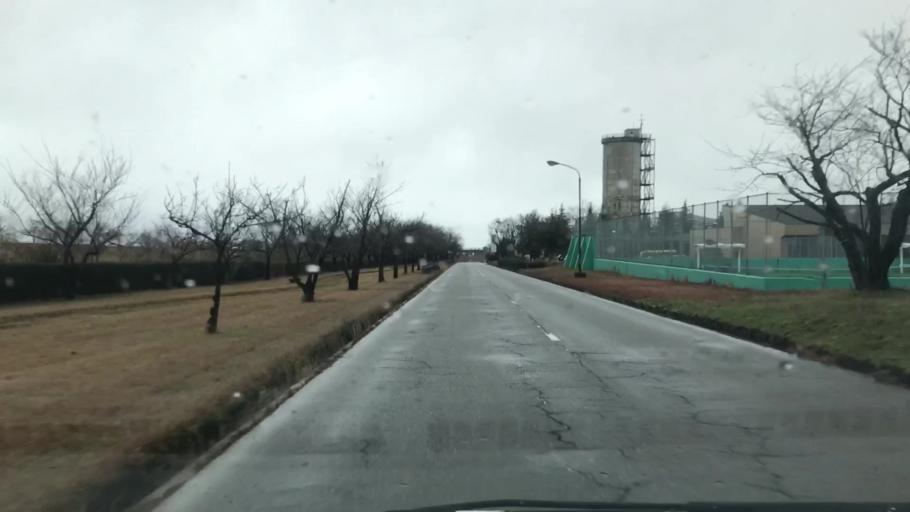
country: JP
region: Toyama
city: Kamiichi
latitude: 36.6225
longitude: 137.3033
